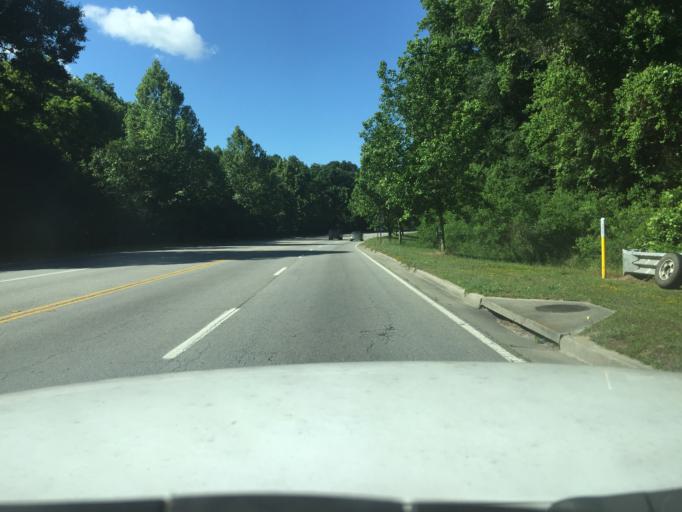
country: US
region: Georgia
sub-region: Chatham County
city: Garden City
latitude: 32.0610
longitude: -81.1606
